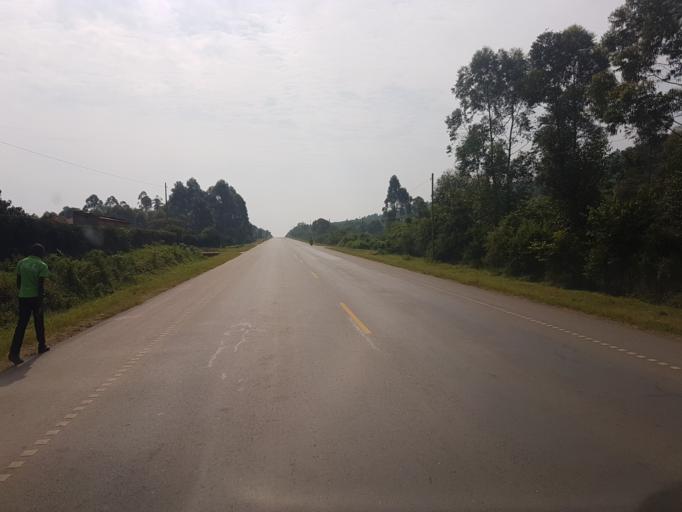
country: UG
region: Western Region
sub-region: Sheema District
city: Kibingo
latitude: -0.6397
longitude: 30.5090
